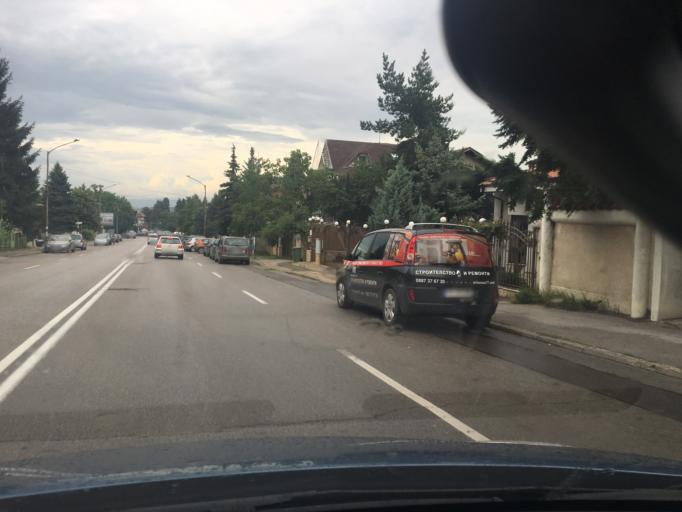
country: BG
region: Sofia-Capital
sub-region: Stolichna Obshtina
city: Sofia
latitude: 42.6563
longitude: 23.2653
